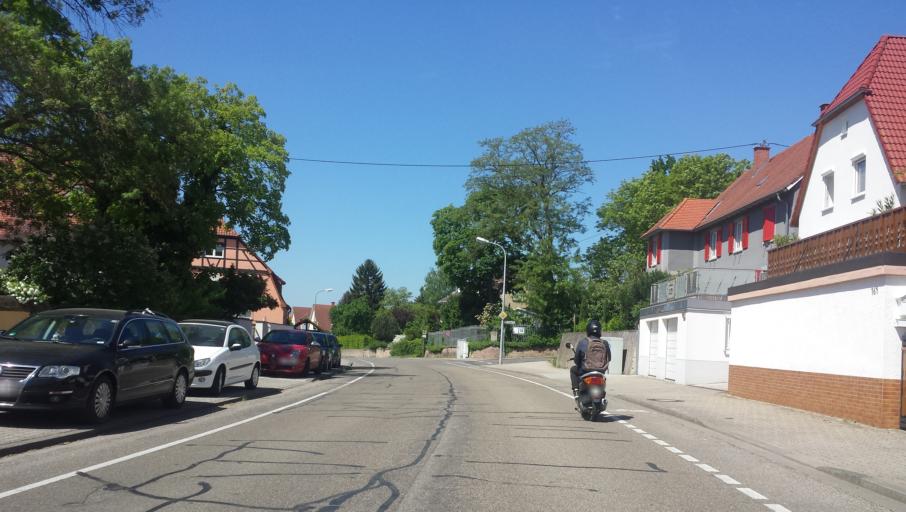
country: DE
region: Rheinland-Pfalz
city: Bochingen
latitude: 49.2105
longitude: 8.0867
